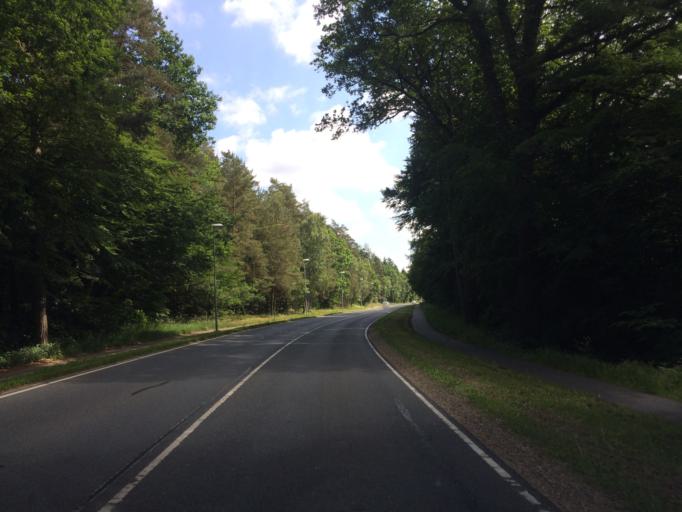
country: DK
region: Central Jutland
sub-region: Silkeborg Kommune
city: Silkeborg
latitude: 56.1631
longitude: 9.5213
